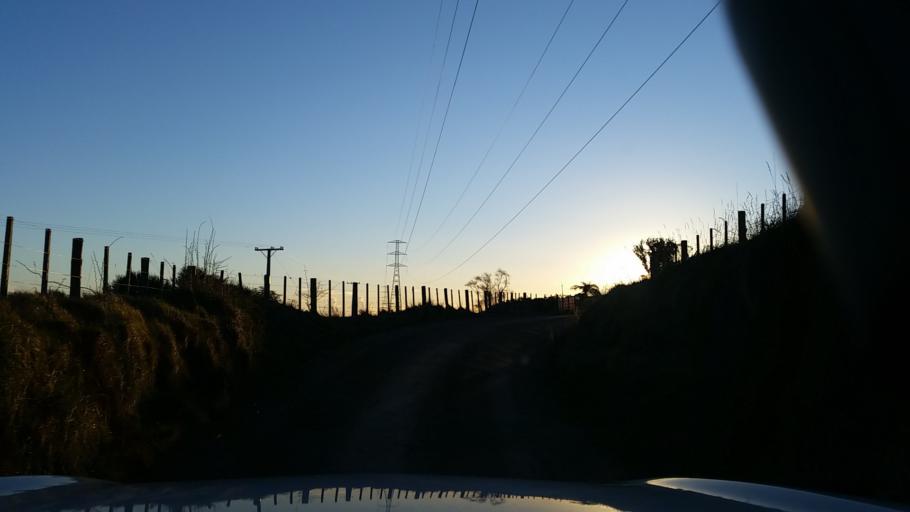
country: NZ
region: Manawatu-Wanganui
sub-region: Wanganui District
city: Wanganui
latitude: -39.7996
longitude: 174.8007
